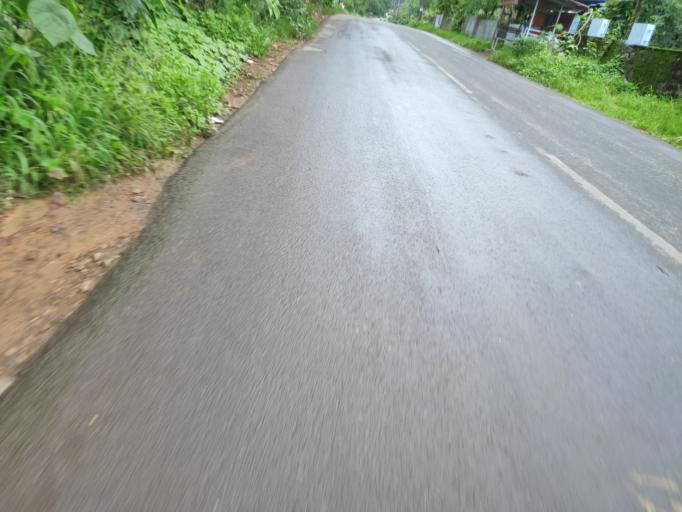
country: IN
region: Kerala
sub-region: Malappuram
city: Manjeri
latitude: 11.2255
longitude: 76.2691
